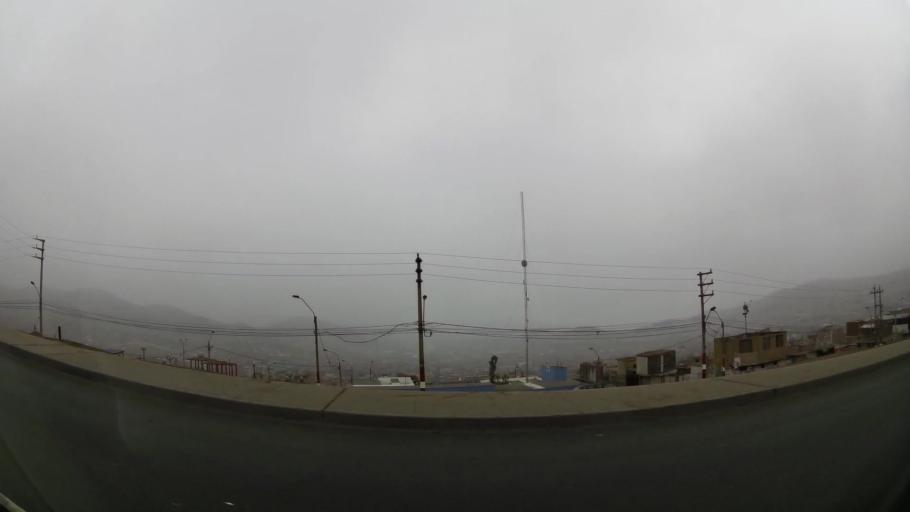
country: PE
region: Lima
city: Ventanilla
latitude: -11.8497
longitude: -77.1242
